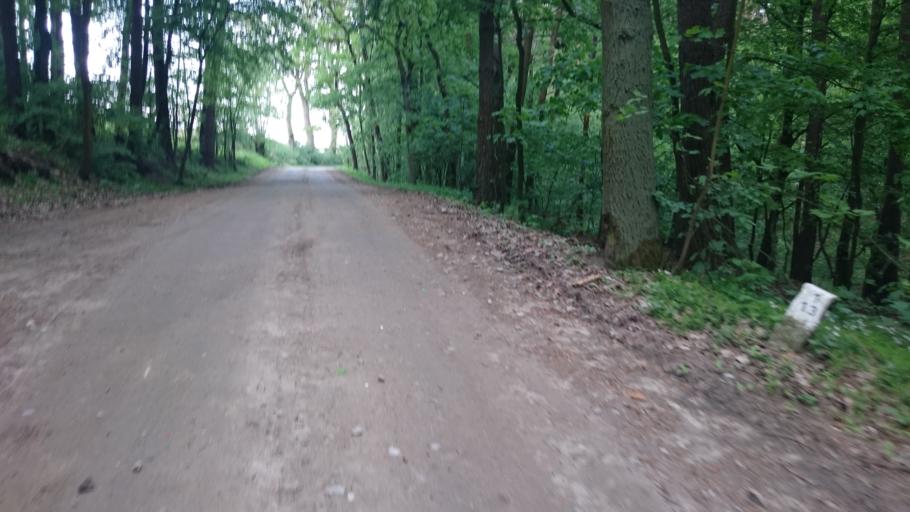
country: PL
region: Kujawsko-Pomorskie
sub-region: Grudziadz
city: Grudziadz
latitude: 53.4542
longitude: 18.8293
